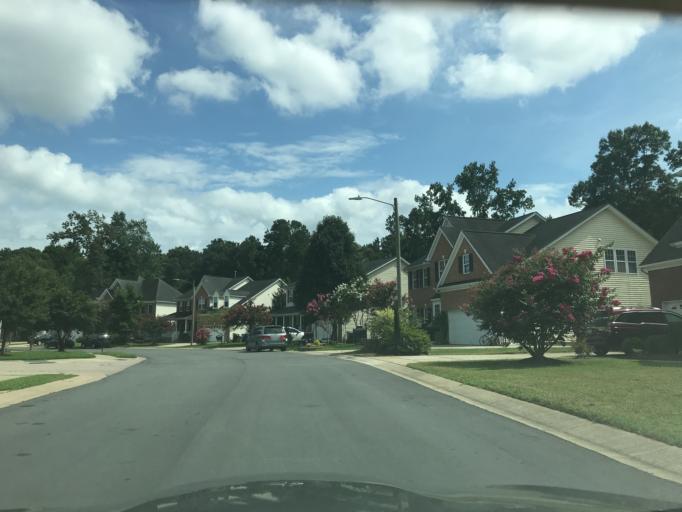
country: US
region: North Carolina
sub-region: Wake County
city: Rolesville
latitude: 35.8915
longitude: -78.5380
